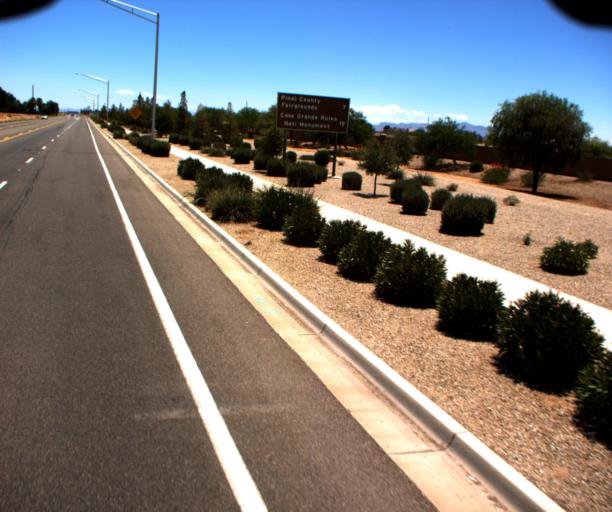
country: US
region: Arizona
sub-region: Pinal County
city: Casa Grande
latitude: 32.8796
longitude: -111.6762
